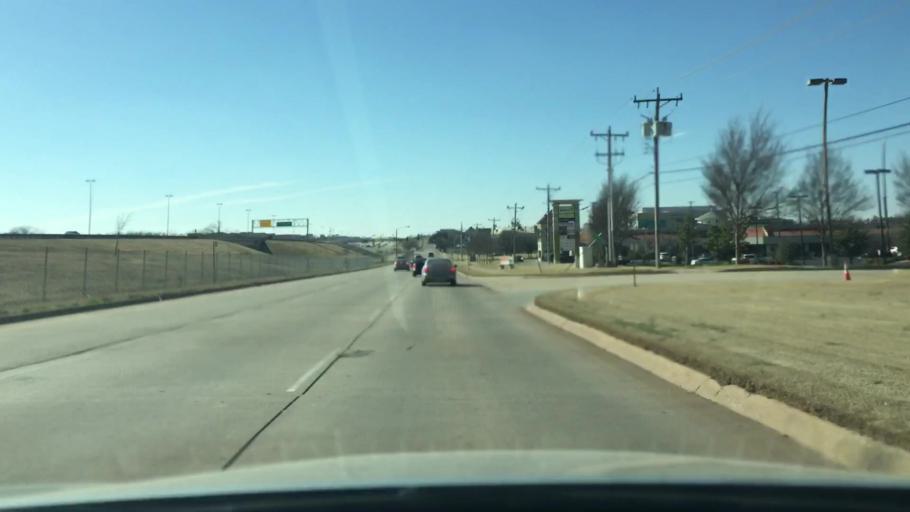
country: US
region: Oklahoma
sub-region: Oklahoma County
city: The Village
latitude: 35.6102
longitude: -97.6001
